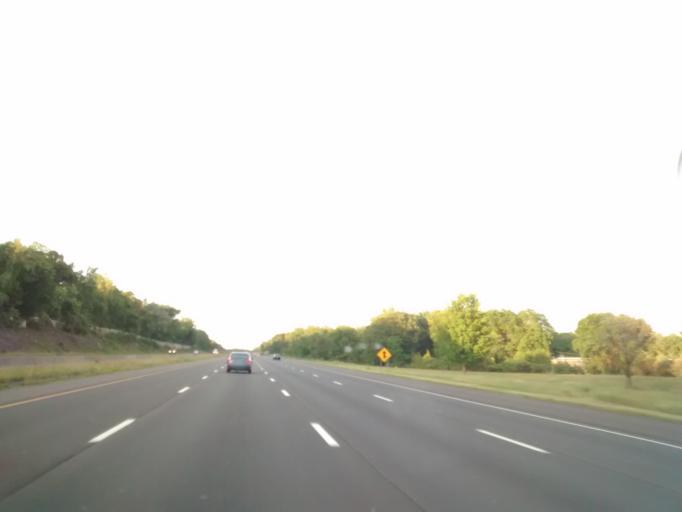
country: US
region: Connecticut
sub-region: Tolland County
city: Rockville
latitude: 41.8354
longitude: -72.4605
